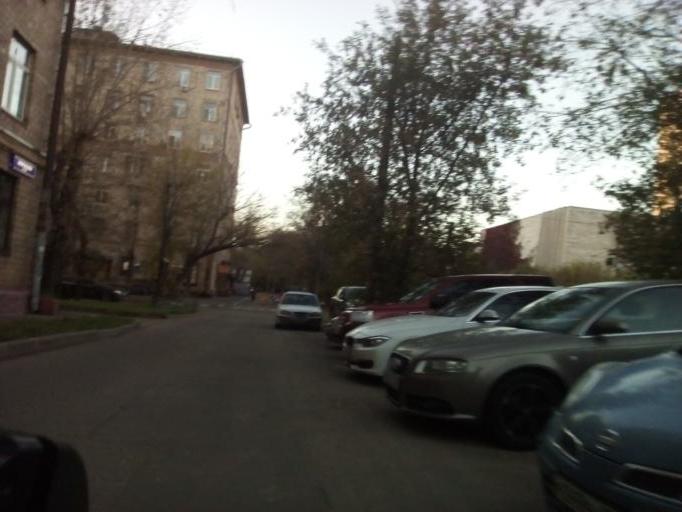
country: RU
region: Moscow
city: Sokol
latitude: 55.8036
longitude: 37.4974
